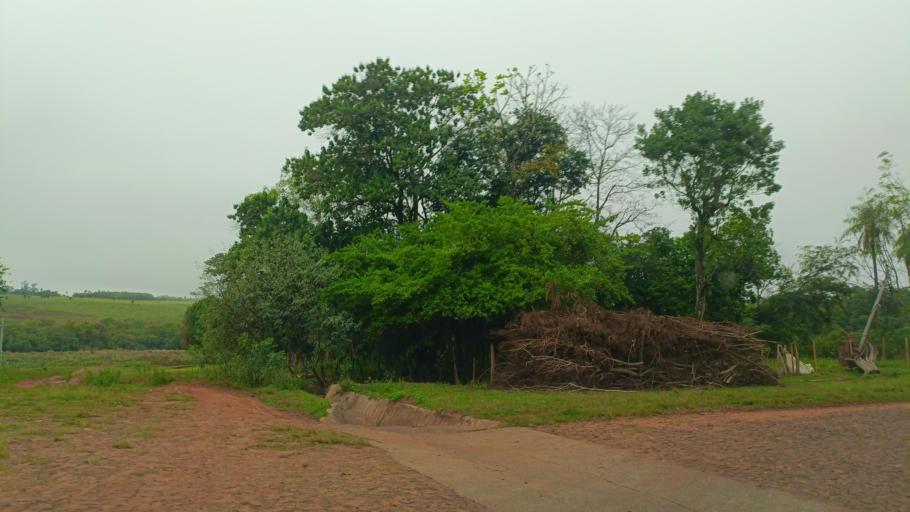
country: PY
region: Misiones
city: Santa Maria
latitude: -26.8630
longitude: -57.0108
